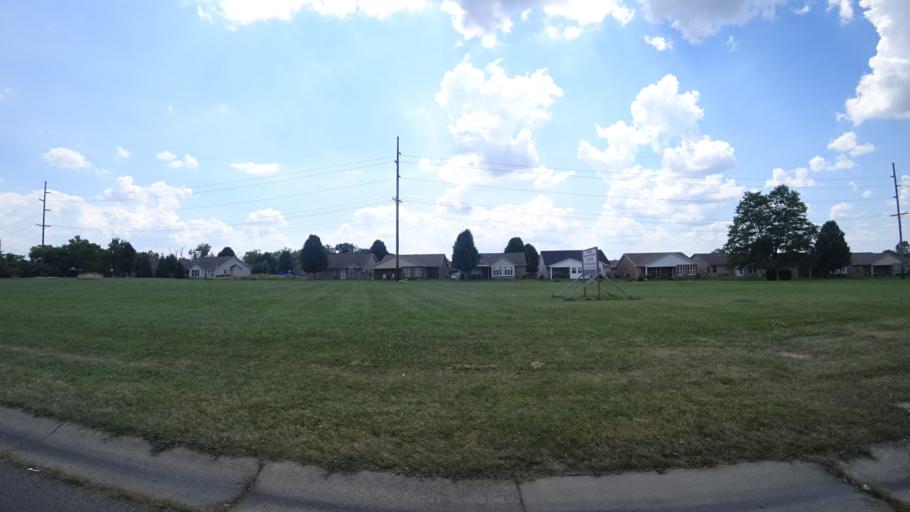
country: US
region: Ohio
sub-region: Butler County
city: New Miami
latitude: 39.4218
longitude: -84.5538
